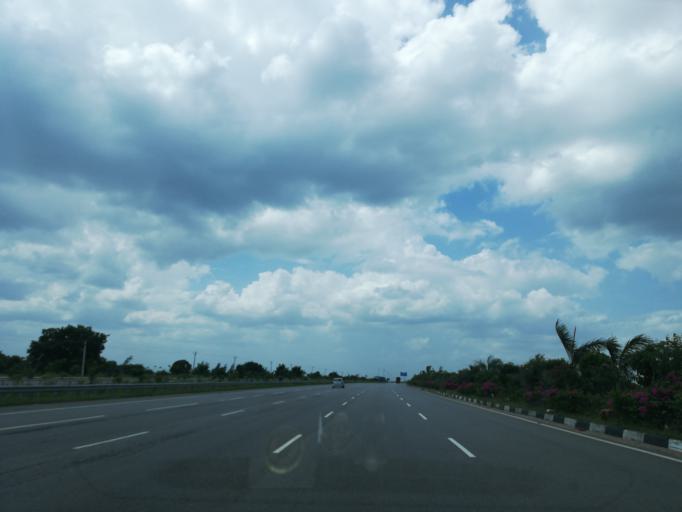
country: IN
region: Telangana
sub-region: Medak
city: Serilingampalle
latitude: 17.4560
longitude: 78.2520
